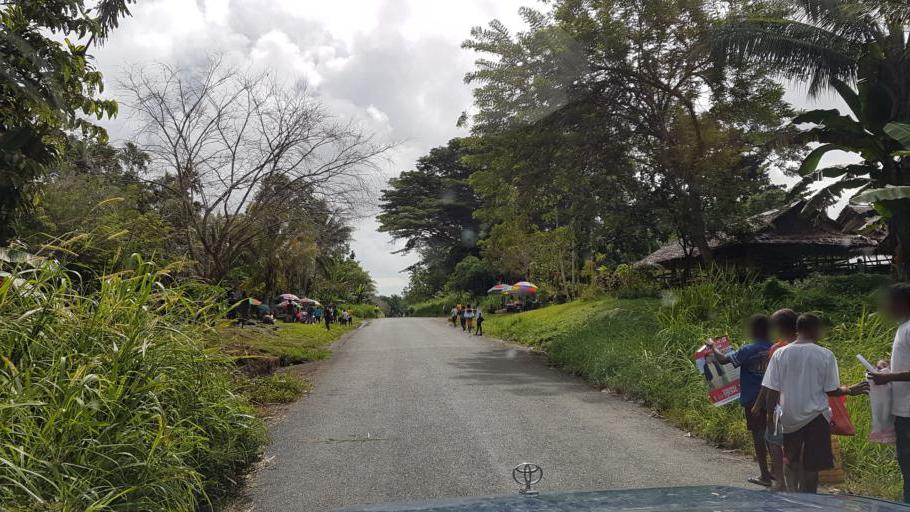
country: PG
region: Northern Province
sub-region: Sohe
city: Popondetta
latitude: -8.8281
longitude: 148.0664
